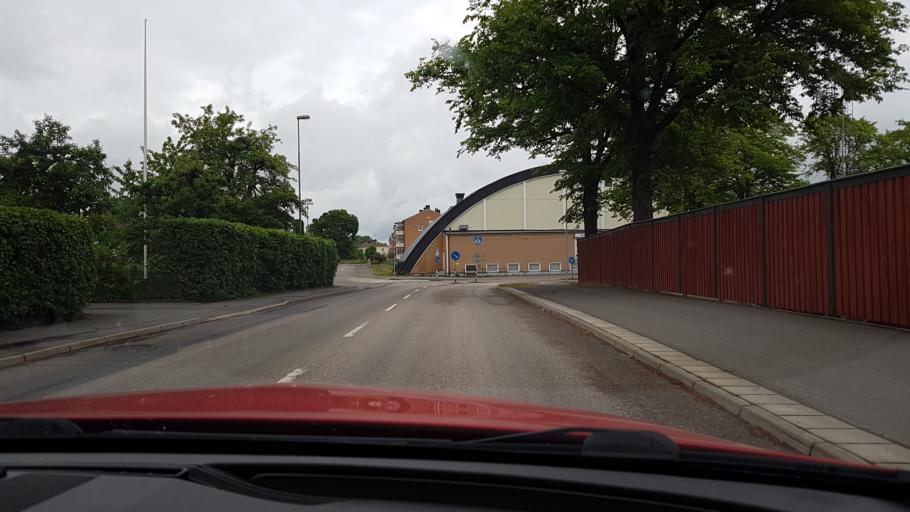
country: SE
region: Vaestra Goetaland
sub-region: Skovde Kommun
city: Skoevde
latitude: 58.3789
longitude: 13.8390
